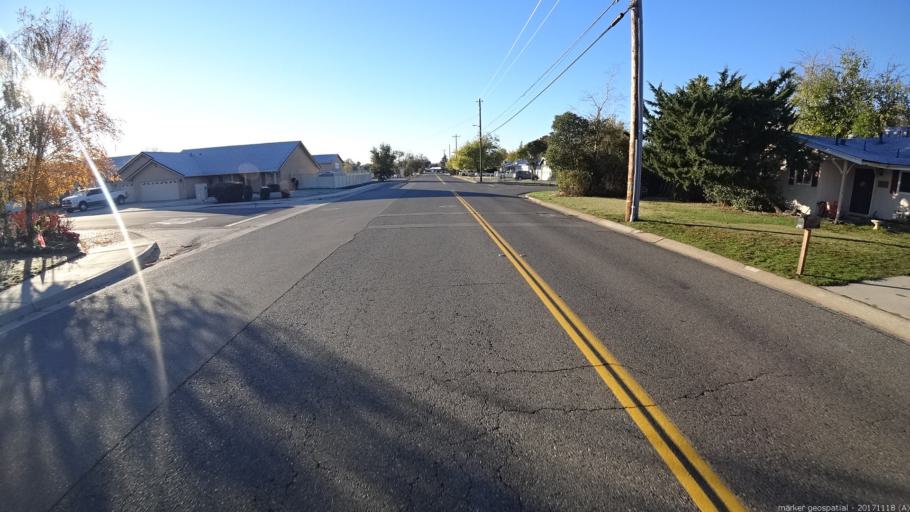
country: US
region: California
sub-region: Shasta County
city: Cottonwood
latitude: 40.3942
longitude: -122.2891
